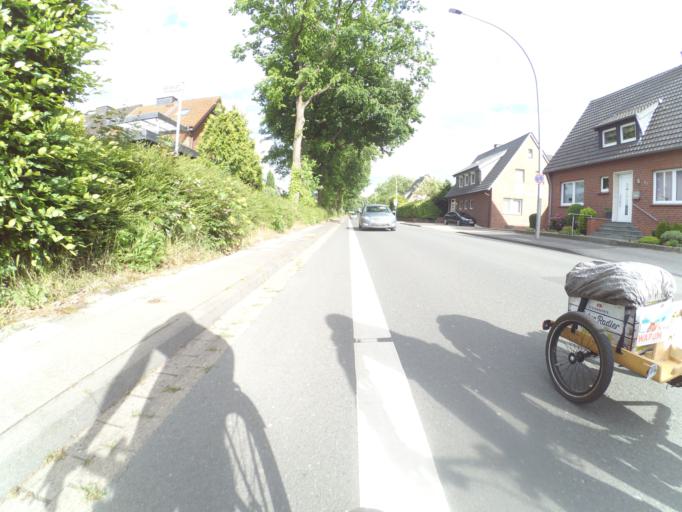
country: DE
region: North Rhine-Westphalia
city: Ibbenburen
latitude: 52.2693
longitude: 7.7253
